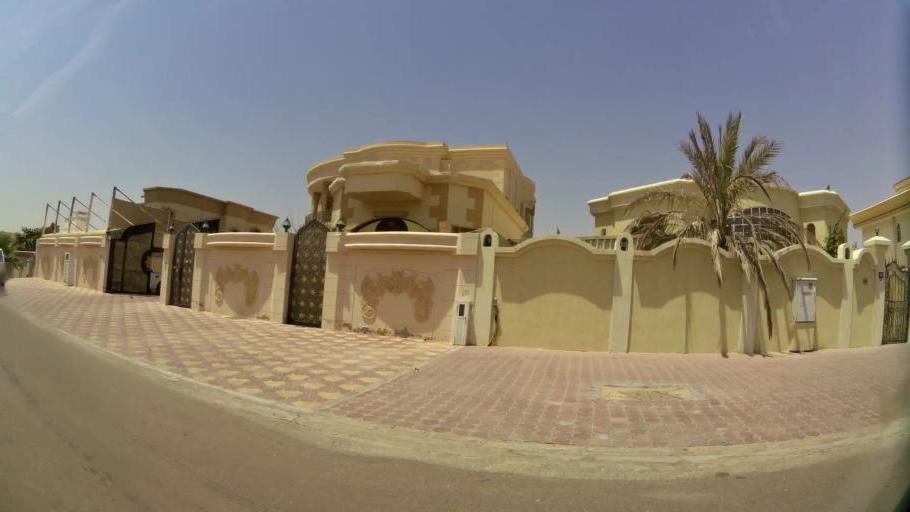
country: AE
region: Ajman
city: Ajman
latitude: 25.4181
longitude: 55.5098
